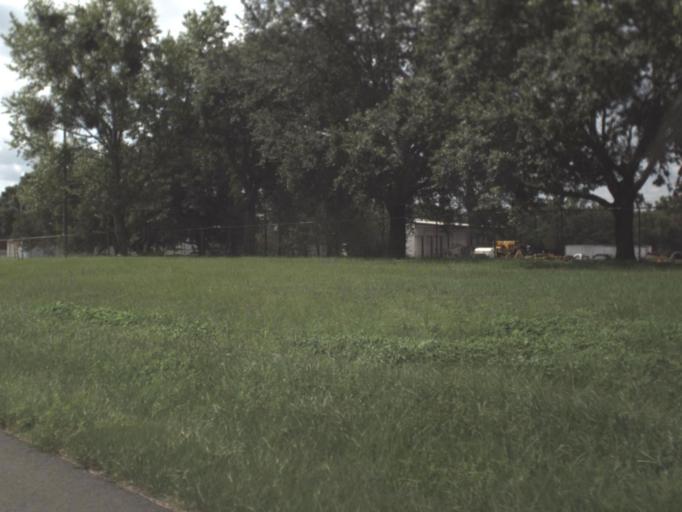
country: US
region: Florida
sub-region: Pasco County
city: Zephyrhills North
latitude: 28.3016
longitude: -82.1517
